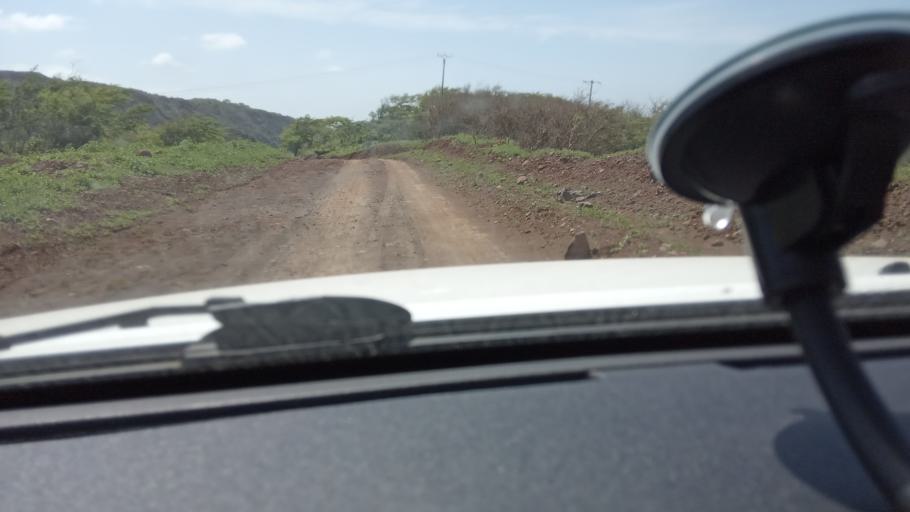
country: CV
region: Santa Catarina
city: Assomada
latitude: 15.0606
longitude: -23.6967
